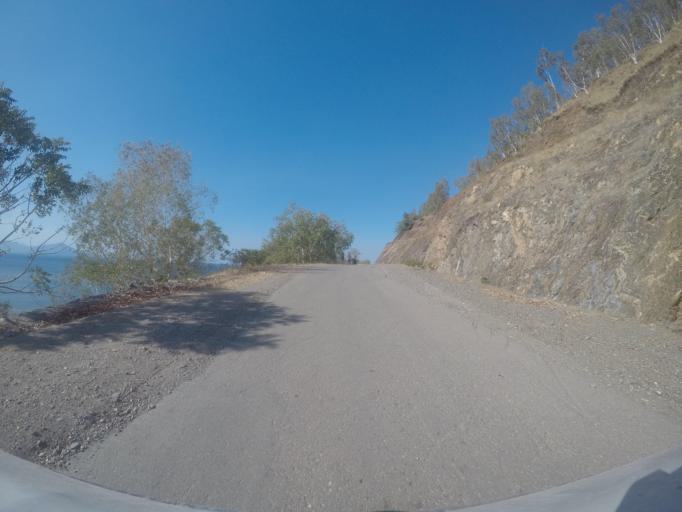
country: TL
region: Dili
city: Dili
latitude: -8.5287
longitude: 125.6261
